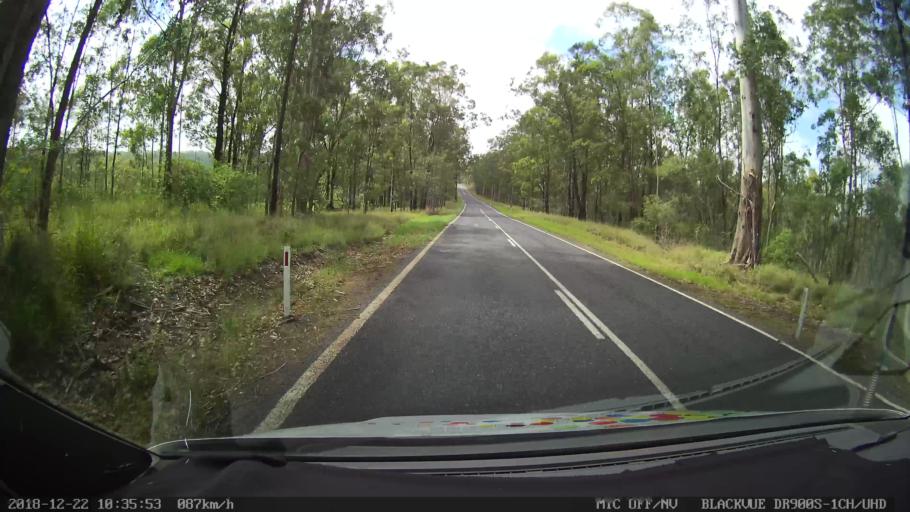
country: AU
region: New South Wales
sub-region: Clarence Valley
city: South Grafton
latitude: -29.6236
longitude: 152.6878
